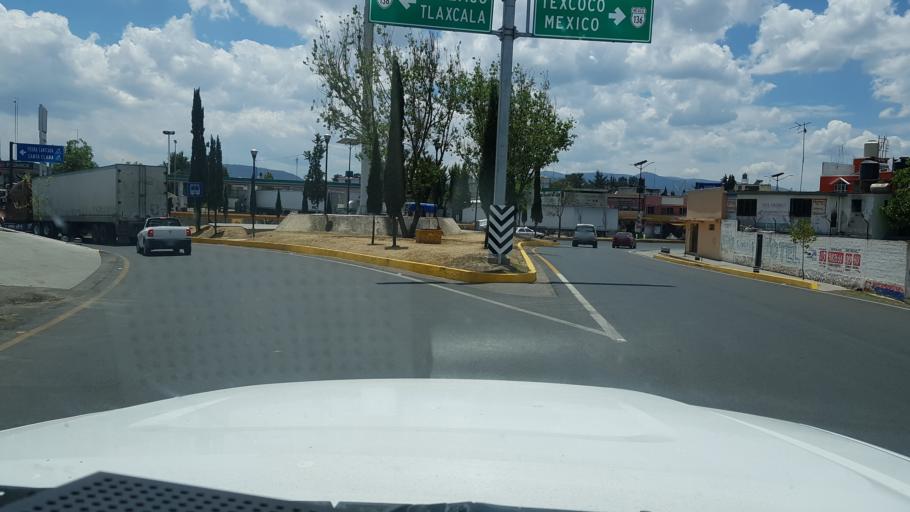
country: MX
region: Hidalgo
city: Calpulalpan
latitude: 19.5933
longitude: -98.5766
